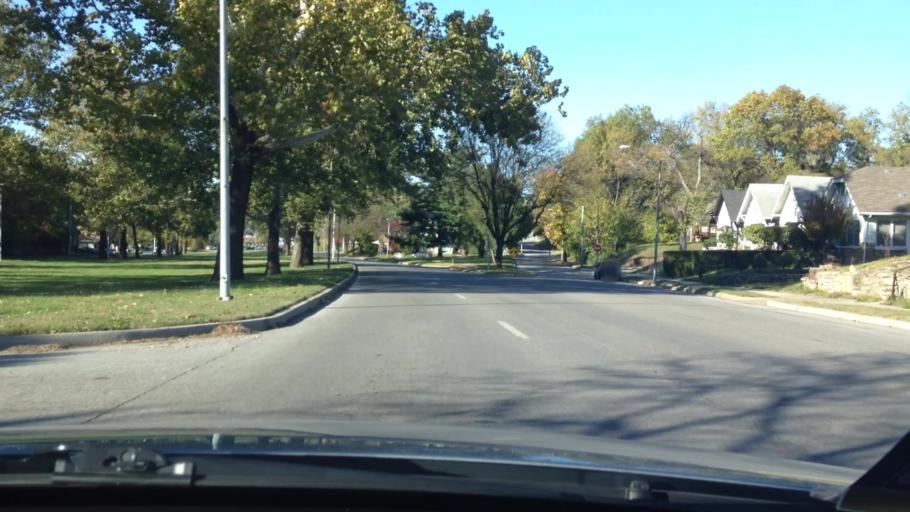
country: US
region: Kansas
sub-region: Johnson County
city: Westwood
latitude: 39.0351
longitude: -94.5671
